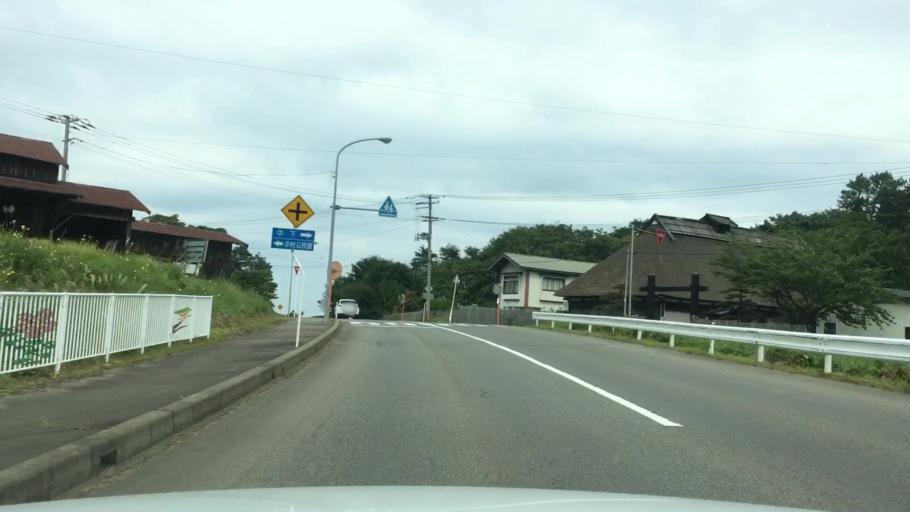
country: JP
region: Aomori
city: Shimokizukuri
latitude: 40.7575
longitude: 140.2306
